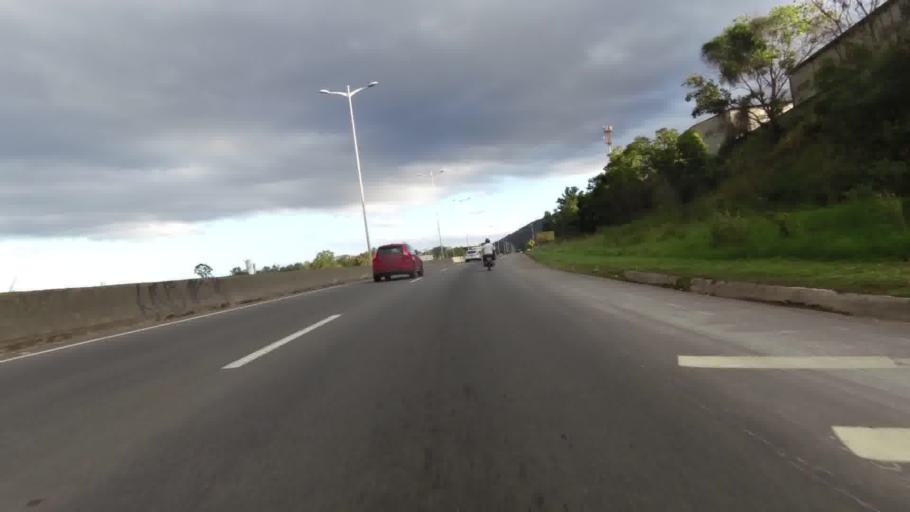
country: BR
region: Espirito Santo
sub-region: Vitoria
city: Vitoria
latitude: -20.2912
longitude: -40.3919
